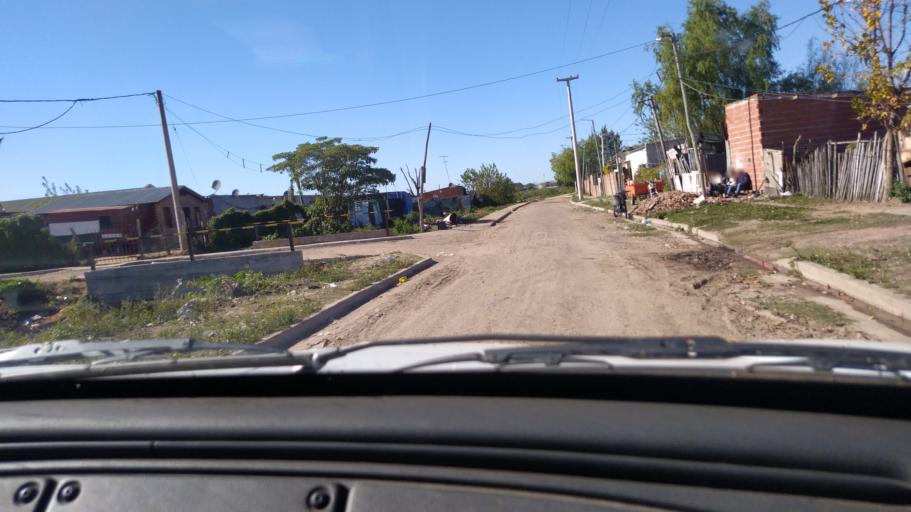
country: AR
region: Corrientes
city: Corrientes
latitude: -27.4989
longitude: -58.8045
